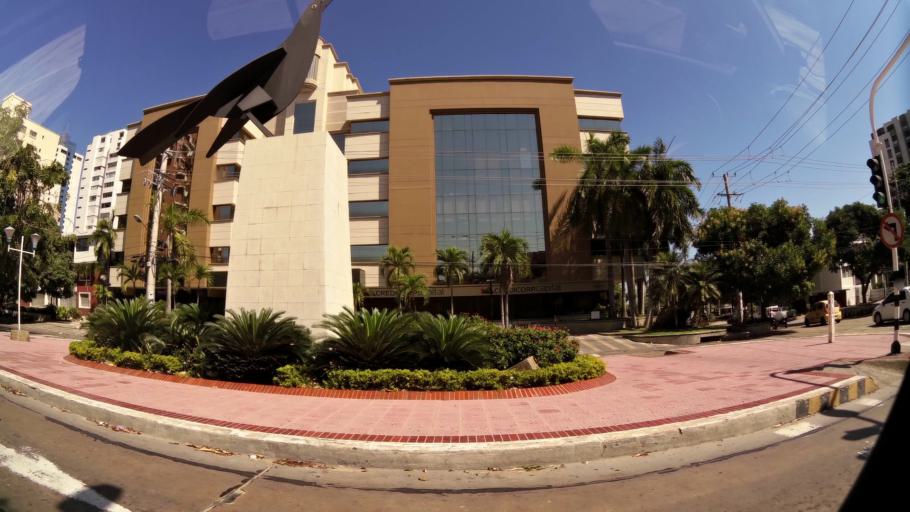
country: CO
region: Atlantico
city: Barranquilla
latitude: 11.0017
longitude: -74.8100
